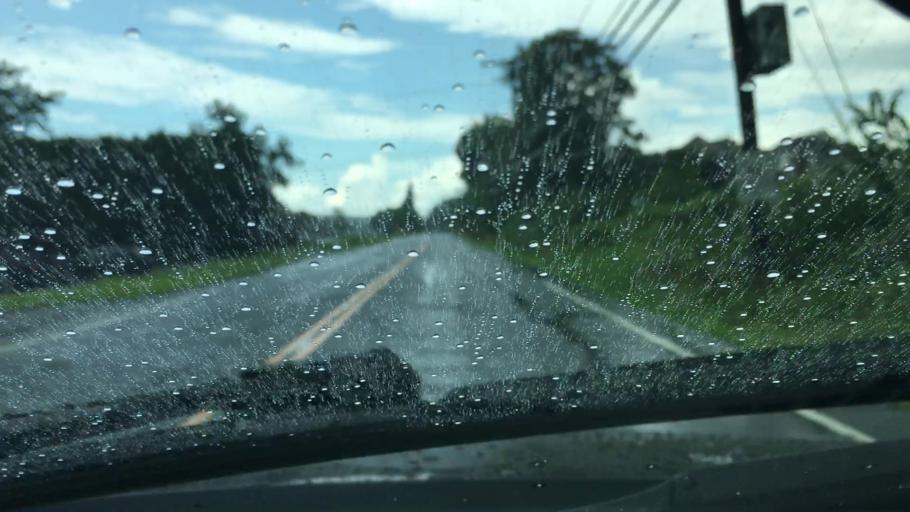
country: US
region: Connecticut
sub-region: Tolland County
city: Ellington
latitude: 41.9238
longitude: -72.4538
